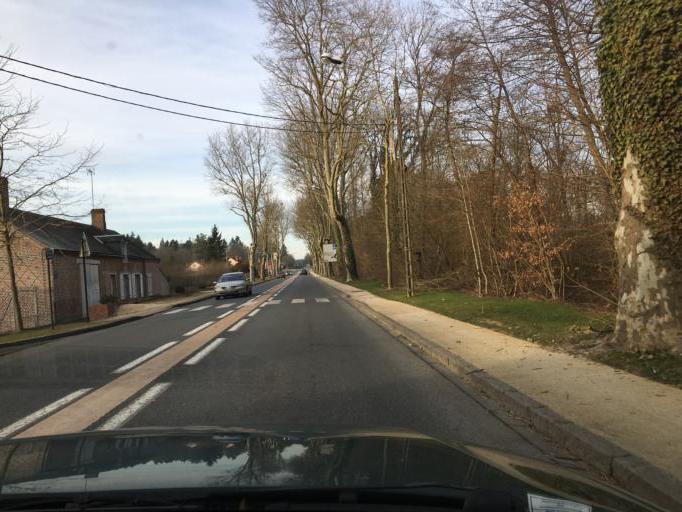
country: FR
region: Centre
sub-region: Departement du Loiret
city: La Ferte-Saint-Aubin
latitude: 47.7269
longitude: 1.9395
